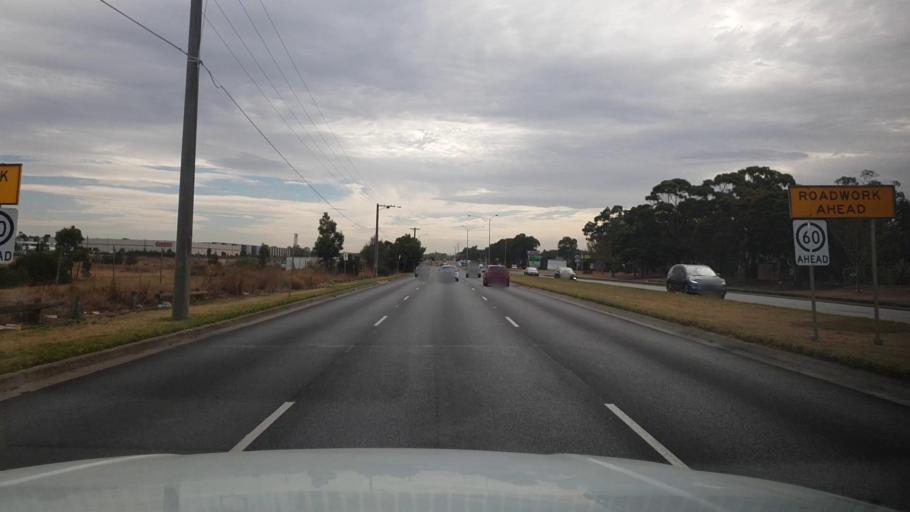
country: AU
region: Victoria
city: Heatherton
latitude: -37.9817
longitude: 145.1100
